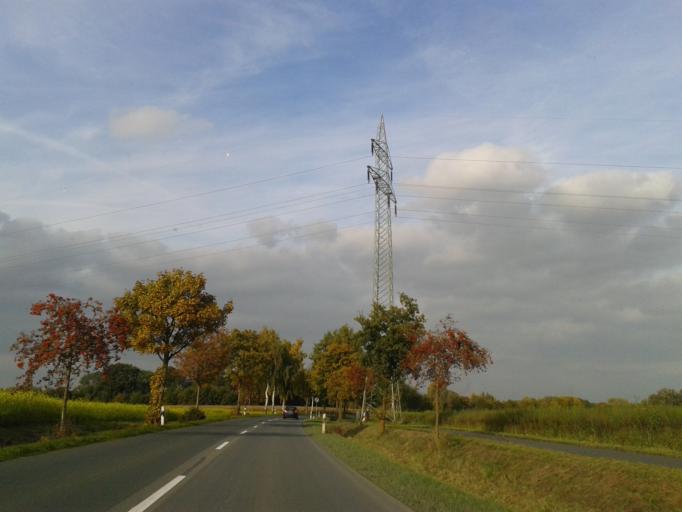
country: DE
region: North Rhine-Westphalia
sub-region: Regierungsbezirk Detmold
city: Hovelhof
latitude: 51.7504
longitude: 8.6576
